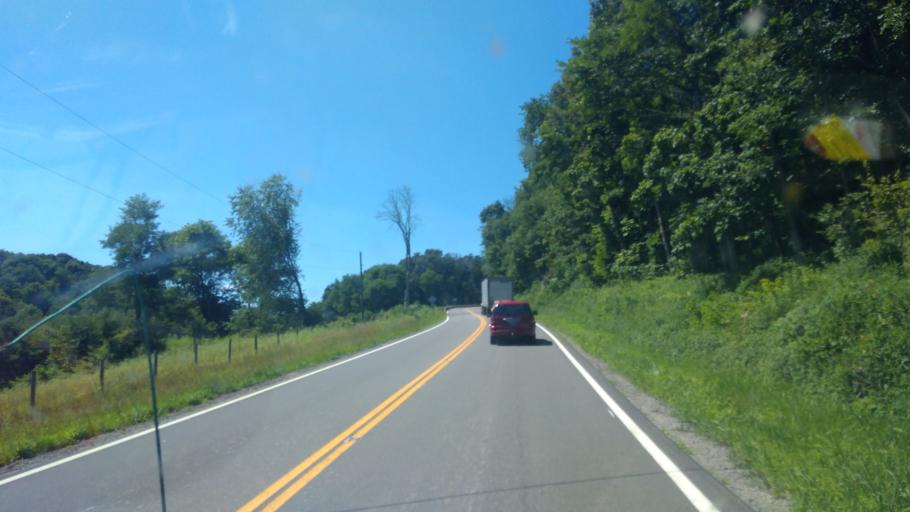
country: US
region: Ohio
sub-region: Carroll County
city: Carrollton
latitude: 40.5028
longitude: -80.9831
